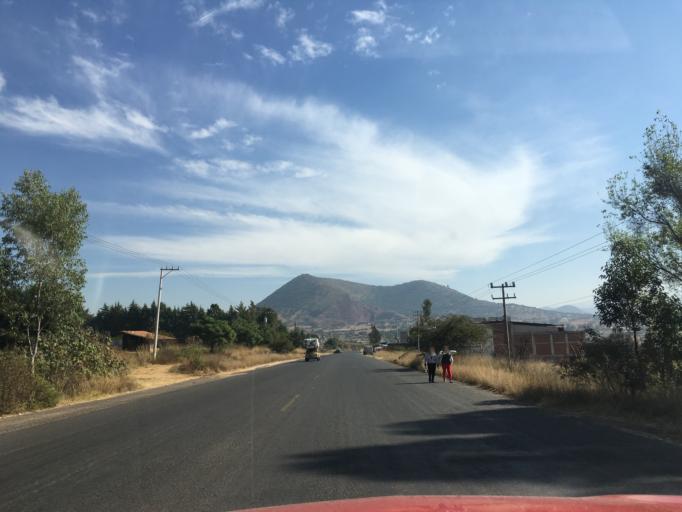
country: MX
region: Michoacan
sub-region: Hidalgo
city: Colonia Aquiles Cordoba Moran
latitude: 19.7106
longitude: -100.5449
